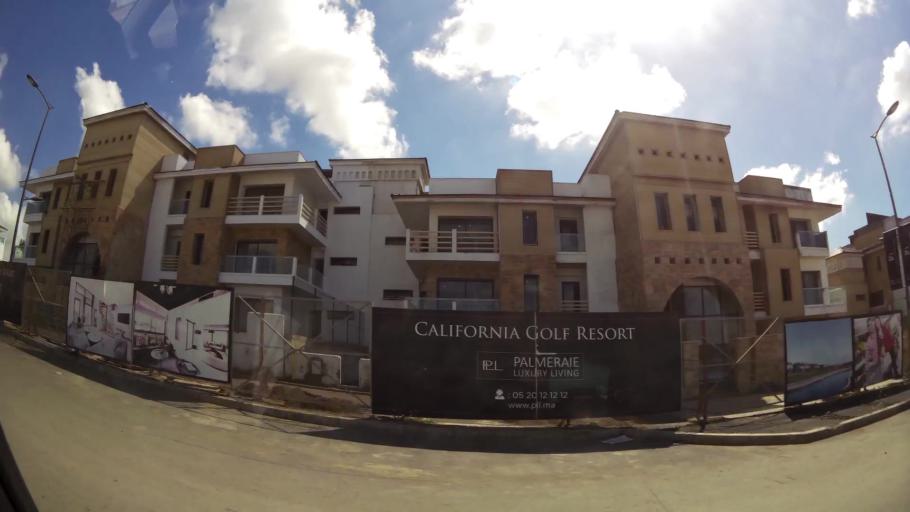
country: MA
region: Grand Casablanca
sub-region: Nouaceur
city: Bouskoura
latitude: 33.4862
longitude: -7.5998
